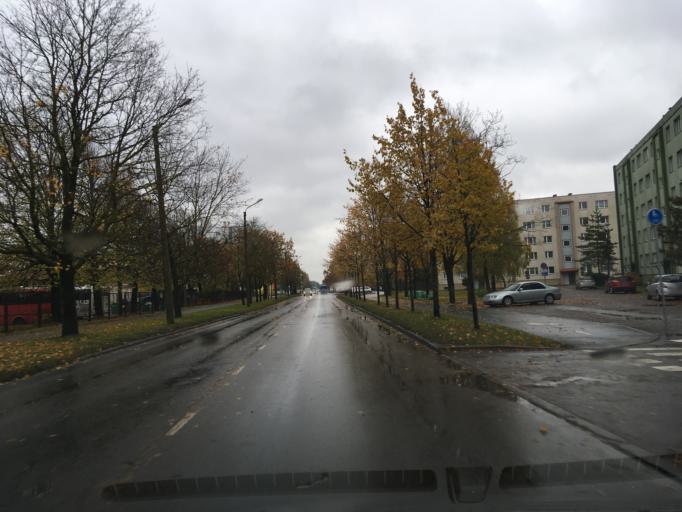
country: EE
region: Paernumaa
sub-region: Paernu linn
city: Parnu
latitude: 58.3717
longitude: 24.5355
